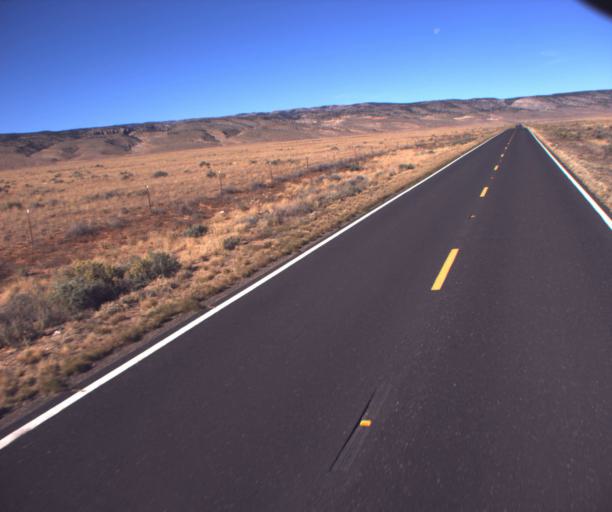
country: US
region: Arizona
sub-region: Coconino County
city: Fredonia
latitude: 36.7208
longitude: -112.0122
